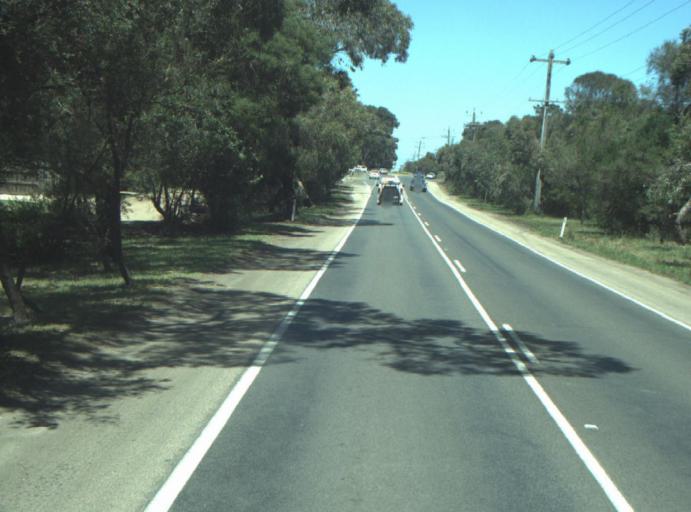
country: AU
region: Victoria
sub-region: Greater Geelong
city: Leopold
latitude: -38.2552
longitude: 144.5361
